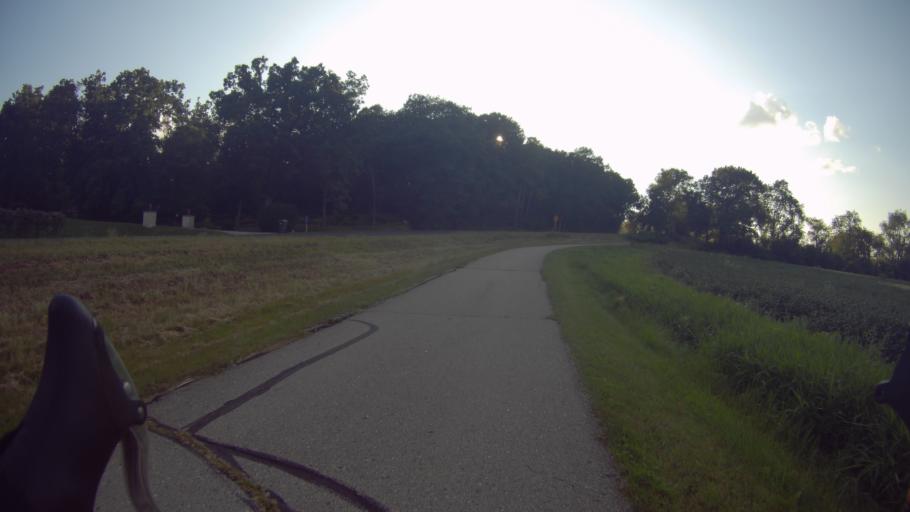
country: US
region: Wisconsin
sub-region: Dane County
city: Monona
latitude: 43.0229
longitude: -89.3708
